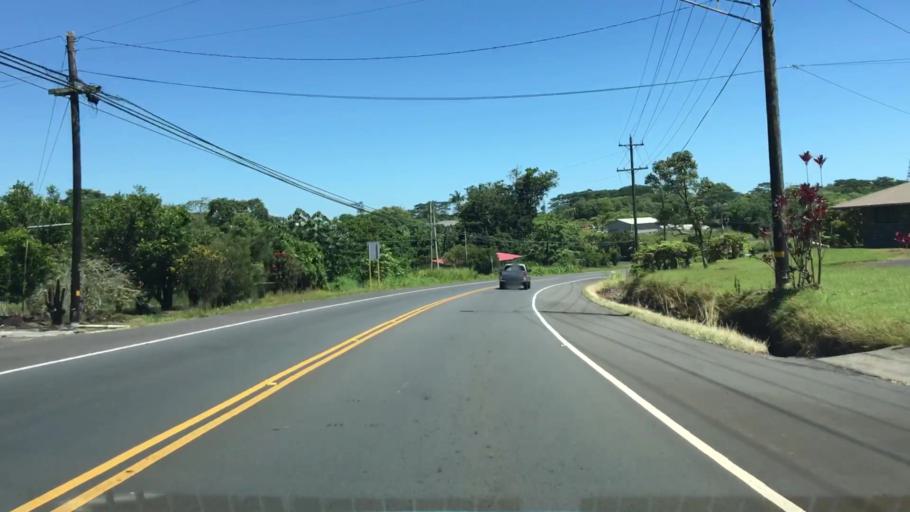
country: US
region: Hawaii
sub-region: Hawaii County
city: Kurtistown
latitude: 19.5880
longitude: -155.0610
